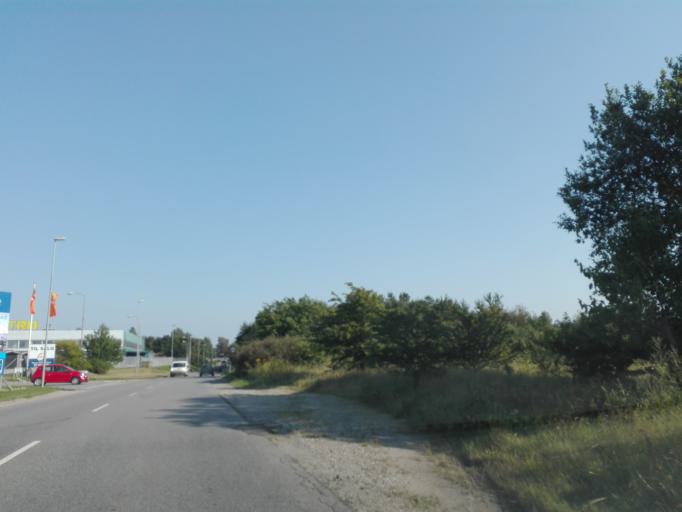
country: DK
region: Central Jutland
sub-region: Arhus Kommune
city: Tranbjerg
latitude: 56.1071
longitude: 10.1324
